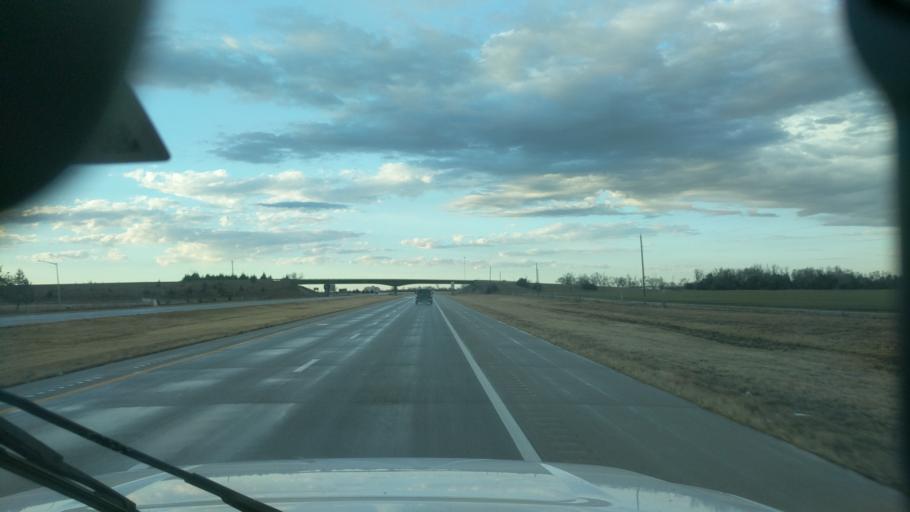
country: US
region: Kansas
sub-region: Harvey County
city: Hesston
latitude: 38.1505
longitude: -97.4242
